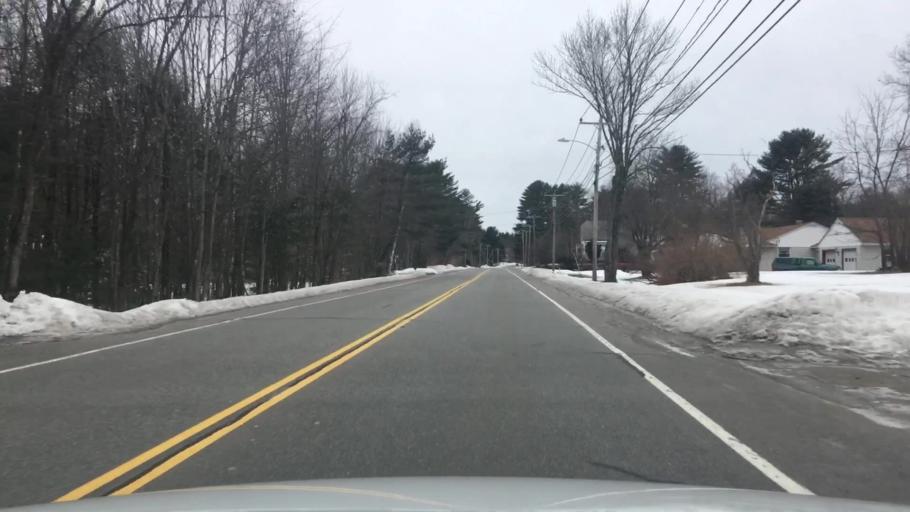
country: US
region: Maine
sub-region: York County
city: Springvale
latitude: 43.4781
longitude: -70.8154
